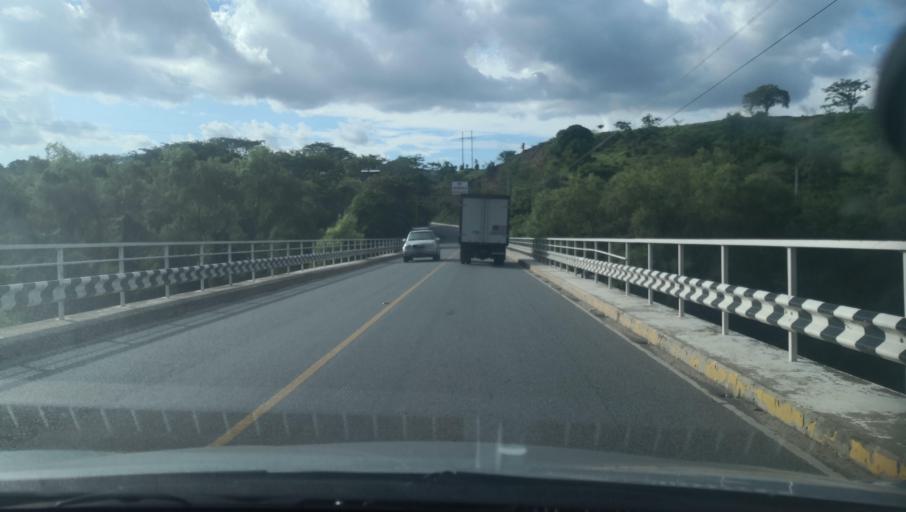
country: NI
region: Nueva Segovia
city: Ocotal
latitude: 13.6113
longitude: -86.4699
